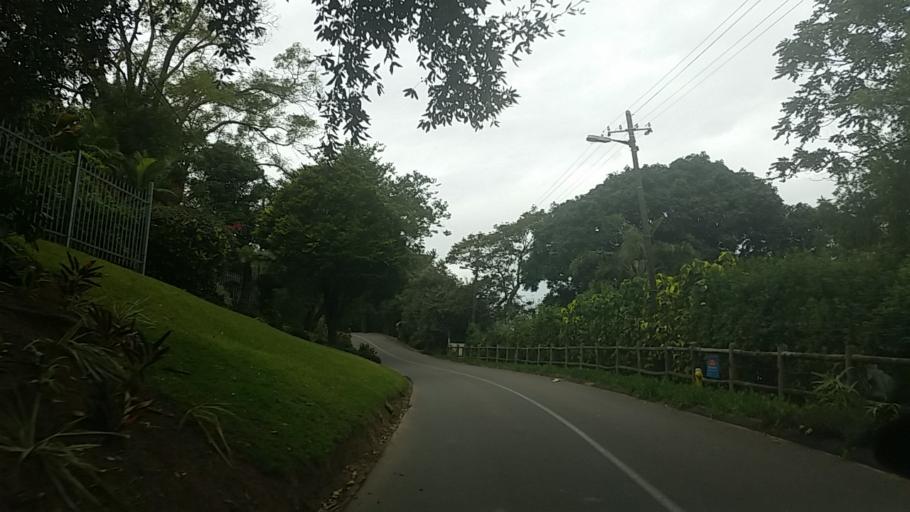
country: ZA
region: KwaZulu-Natal
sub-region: eThekwini Metropolitan Municipality
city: Berea
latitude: -29.8405
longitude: 30.9339
